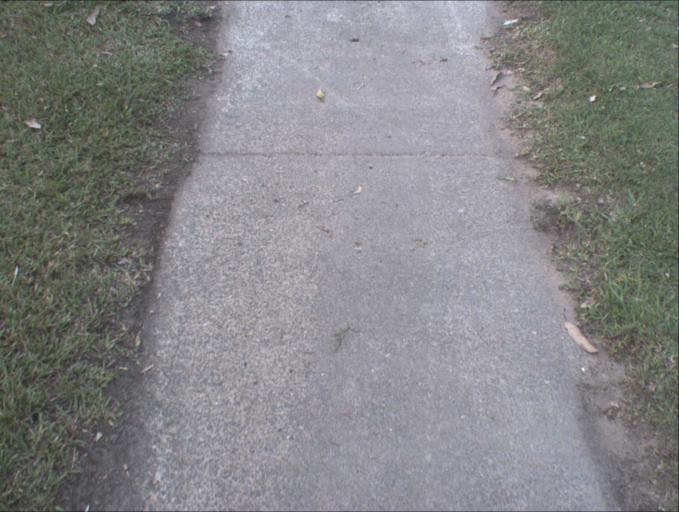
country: AU
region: Queensland
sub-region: Brisbane
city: Forest Lake
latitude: -27.6614
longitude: 152.9931
